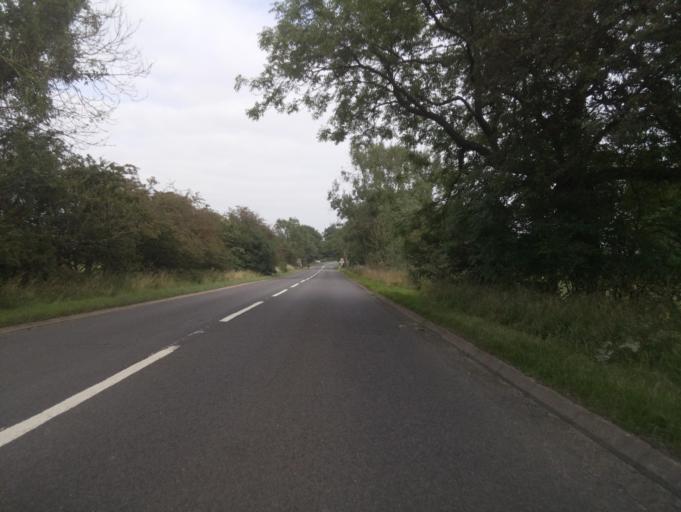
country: GB
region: England
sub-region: Staffordshire
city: Mayfield
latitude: 53.0343
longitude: -1.8126
